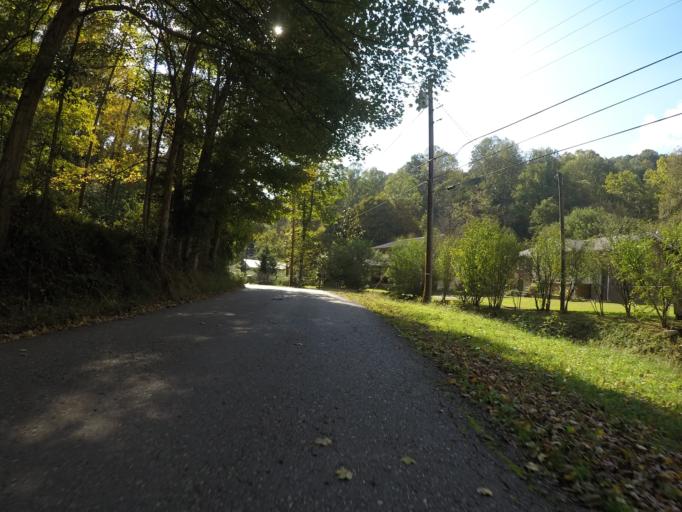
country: US
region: West Virginia
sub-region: Wayne County
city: Lavalette
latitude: 38.3588
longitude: -82.4874
